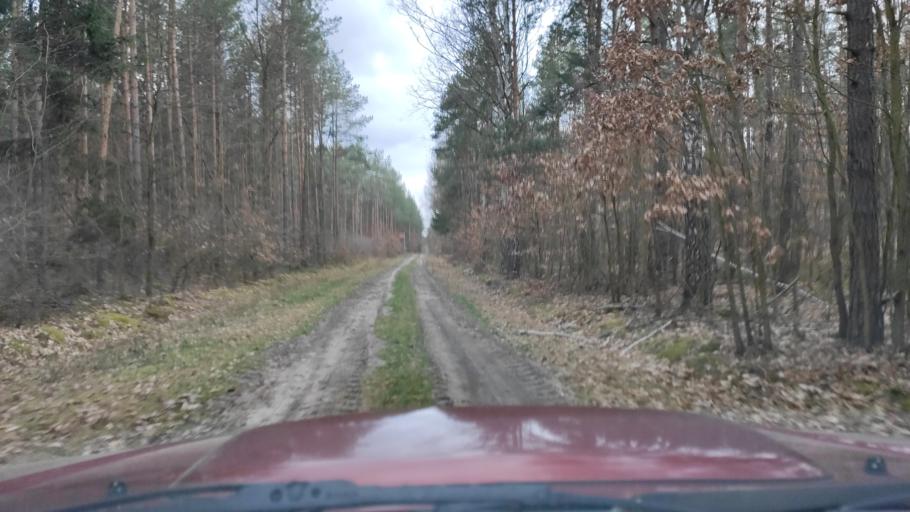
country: PL
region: Masovian Voivodeship
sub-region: Powiat kozienicki
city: Garbatka-Letnisko
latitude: 51.5077
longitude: 21.5517
